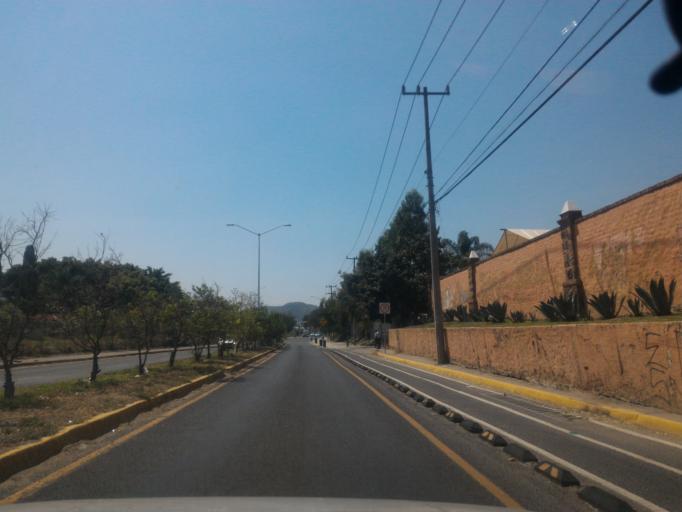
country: MX
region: Jalisco
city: Nicolas R Casillas
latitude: 20.5516
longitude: -103.4570
